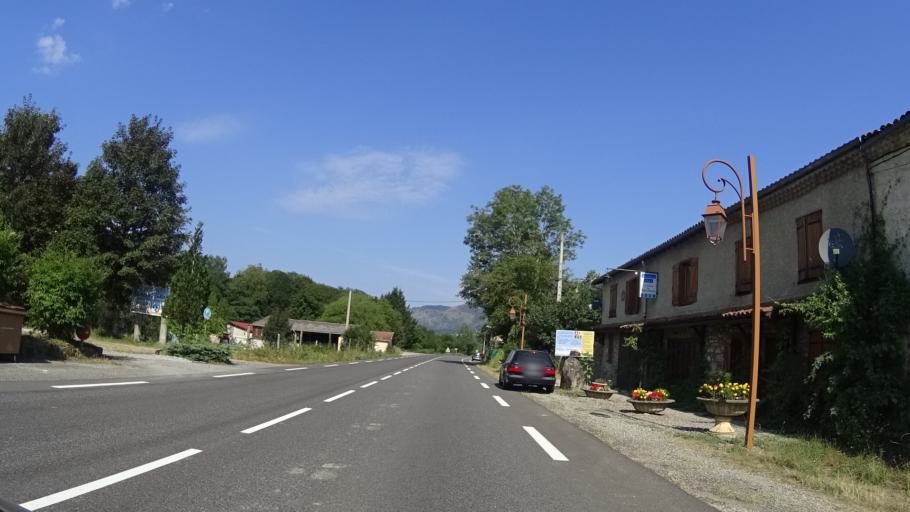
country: FR
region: Midi-Pyrenees
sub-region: Departement de l'Ariege
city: Saint-Paul-de-Jarrat
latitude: 42.9274
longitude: 1.7410
